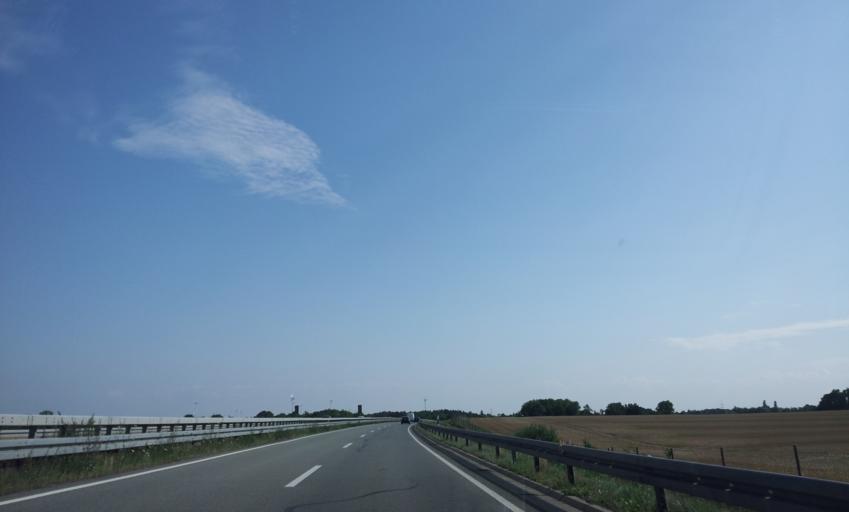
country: DE
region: Mecklenburg-Vorpommern
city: Brandshagen
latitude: 54.2296
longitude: 13.1546
